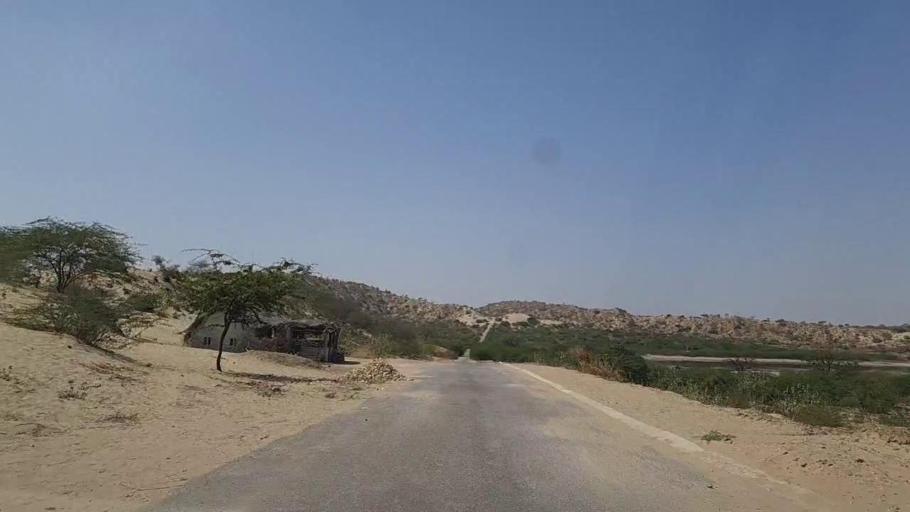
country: PK
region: Sindh
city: Diplo
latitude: 24.5371
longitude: 69.3961
